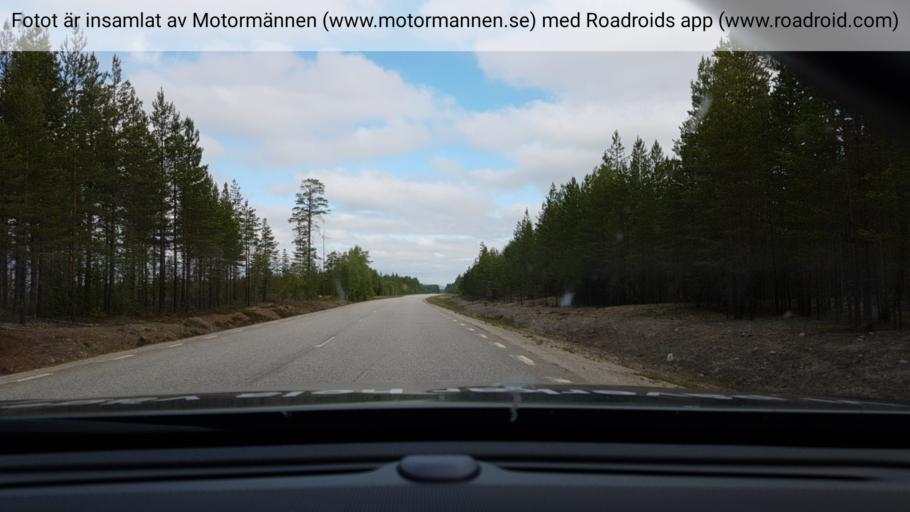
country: SE
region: Vaesterbotten
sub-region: Norsjo Kommun
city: Norsjoe
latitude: 64.5640
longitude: 19.3166
